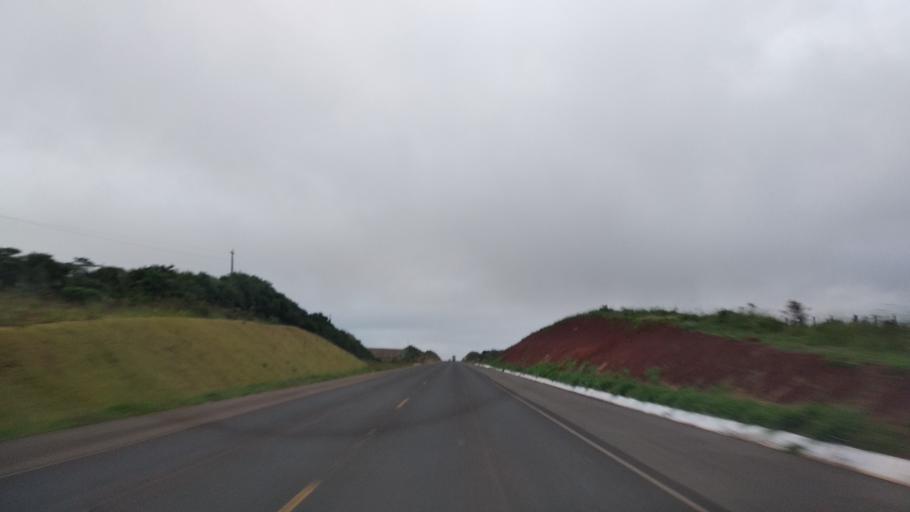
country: BR
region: Santa Catarina
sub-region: Campos Novos
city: Campos Novos
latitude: -27.3820
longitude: -51.0604
